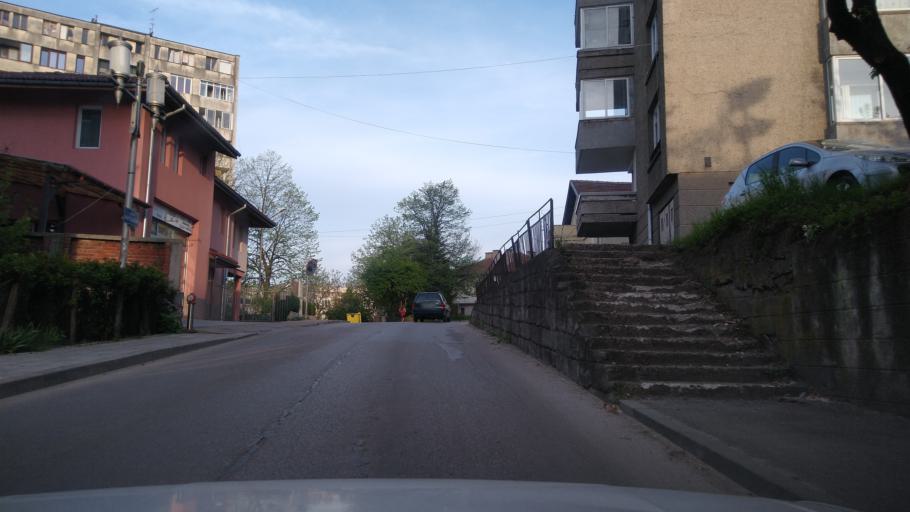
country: BG
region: Gabrovo
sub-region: Obshtina Gabrovo
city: Gabrovo
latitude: 42.8687
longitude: 25.3143
